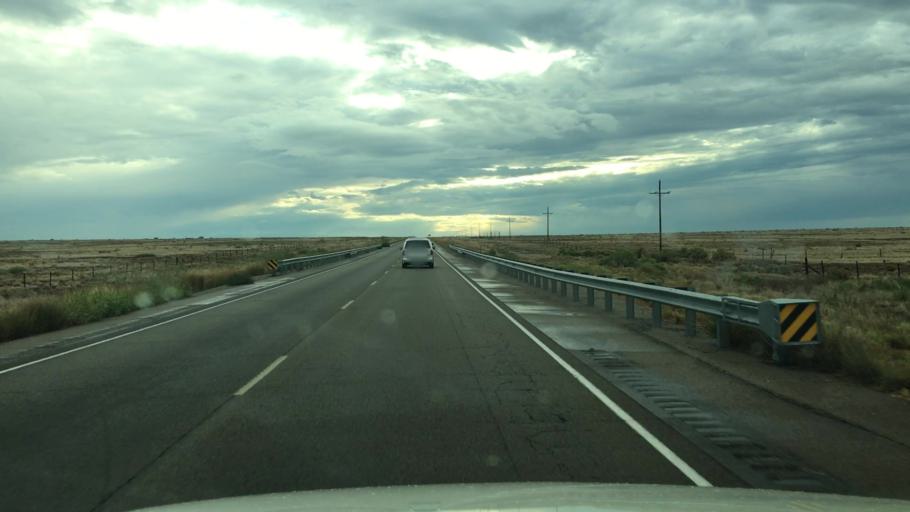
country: US
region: New Mexico
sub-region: Chaves County
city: Roswell
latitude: 33.4038
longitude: -104.3196
